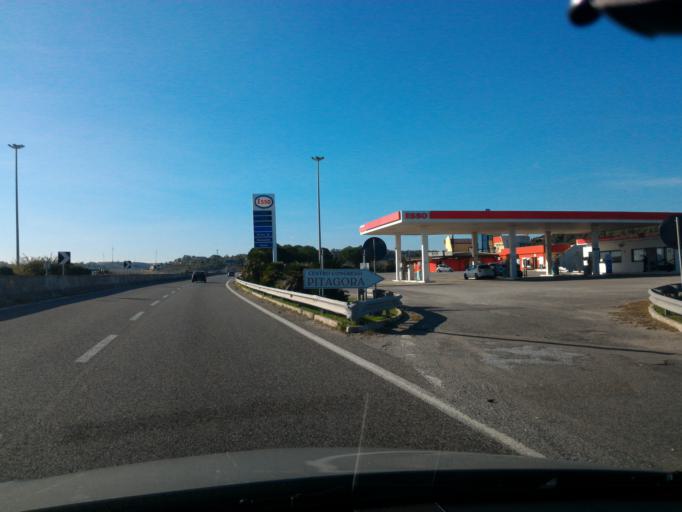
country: IT
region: Calabria
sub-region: Provincia di Crotone
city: Crotone
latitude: 39.1249
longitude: 17.0926
